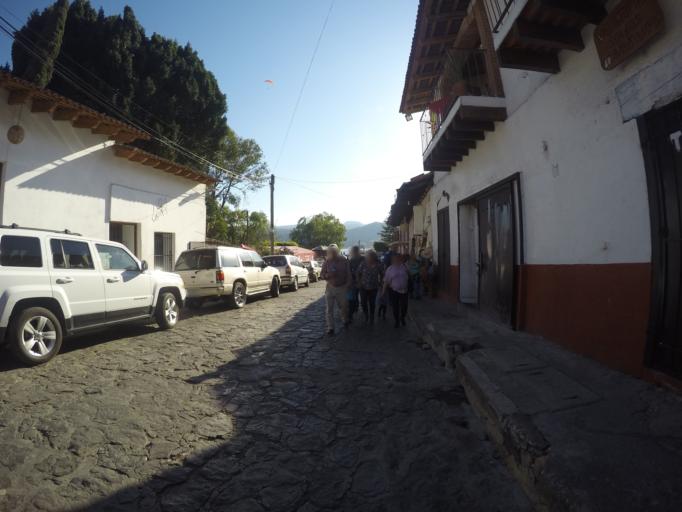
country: MX
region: Mexico
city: Valle de Bravo
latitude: 19.1897
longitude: -100.1301
